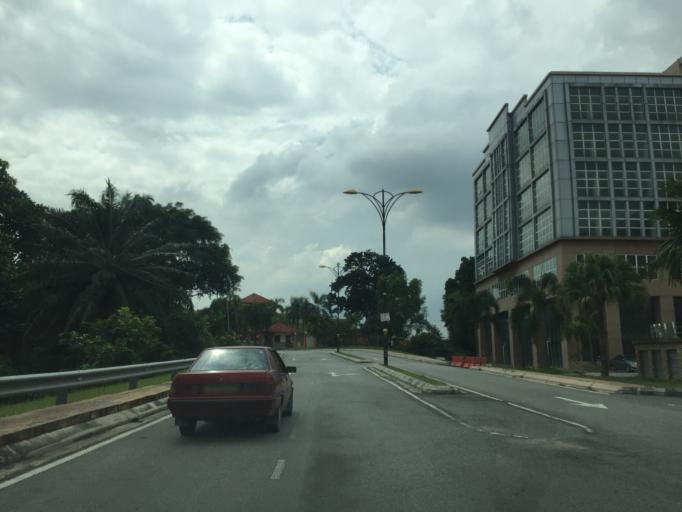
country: MY
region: Selangor
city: Klang
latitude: 3.0416
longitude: 101.4437
